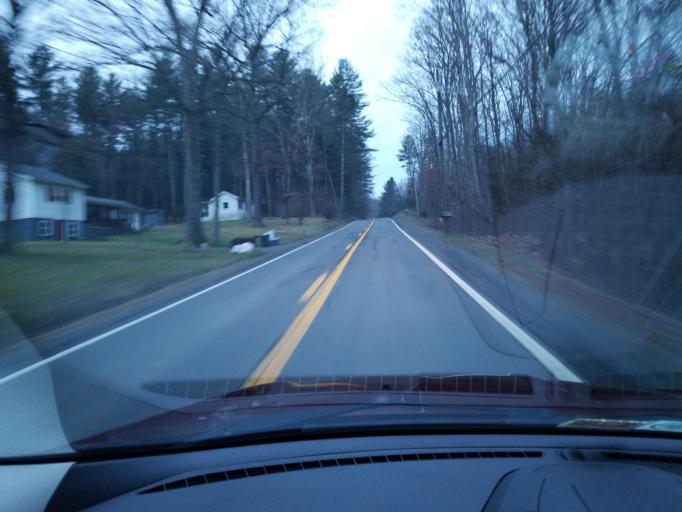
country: US
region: West Virginia
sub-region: Greenbrier County
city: Lewisburg
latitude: 37.7631
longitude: -80.3964
